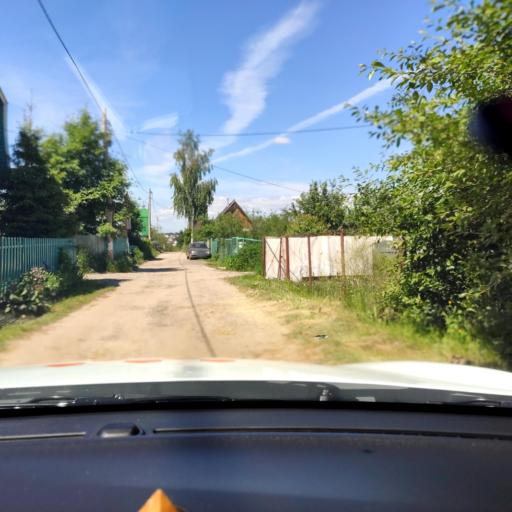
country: RU
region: Tatarstan
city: Vysokaya Gora
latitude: 55.8128
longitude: 49.2840
